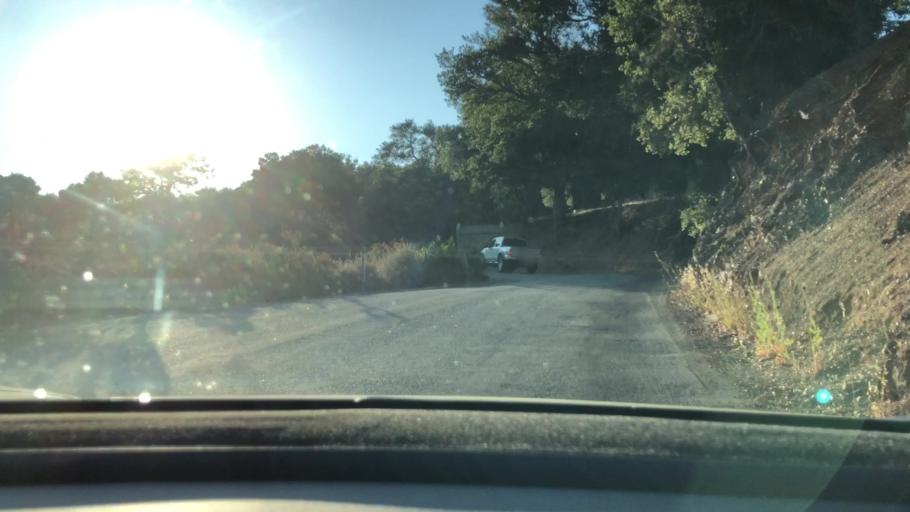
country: US
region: California
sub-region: Santa Clara County
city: Saratoga
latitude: 37.2549
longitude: -122.0613
